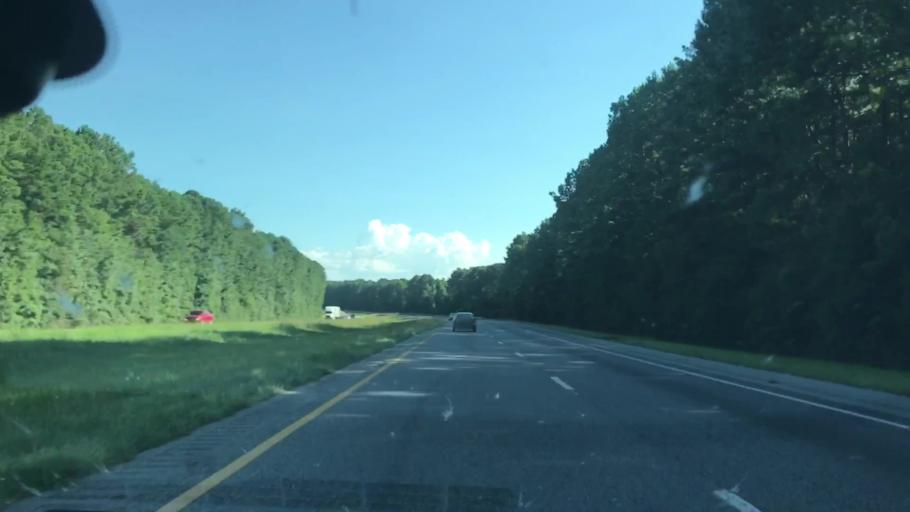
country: US
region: Georgia
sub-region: Harris County
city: Hamilton
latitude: 32.7771
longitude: -85.0208
